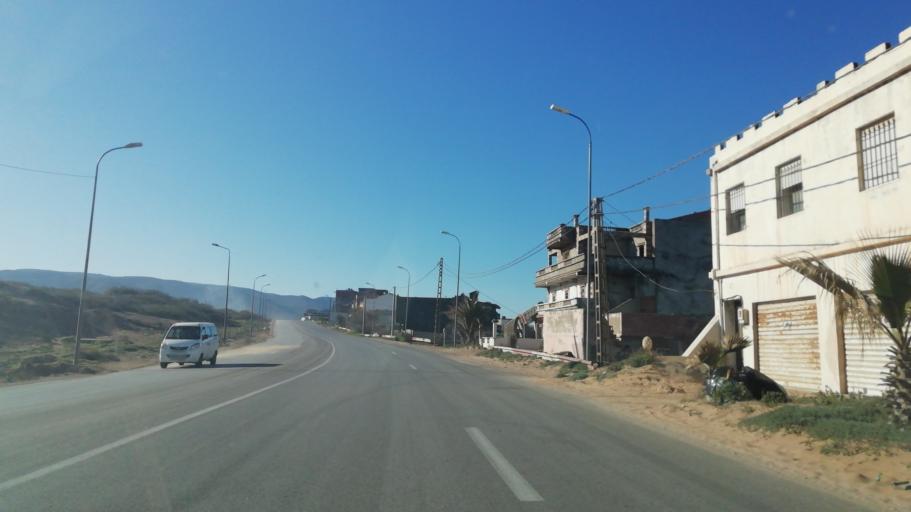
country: DZ
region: Oran
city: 'Ain el Turk
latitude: 35.7359
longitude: -0.8406
